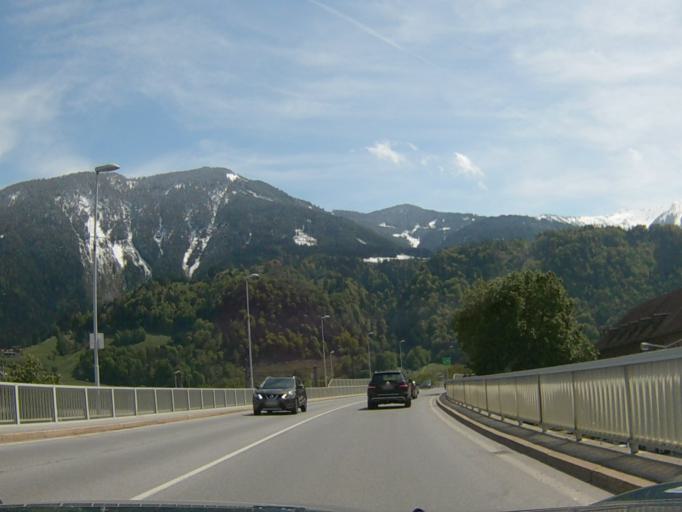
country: AT
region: Tyrol
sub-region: Politischer Bezirk Schwaz
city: Jenbach
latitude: 47.3881
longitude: 11.7743
